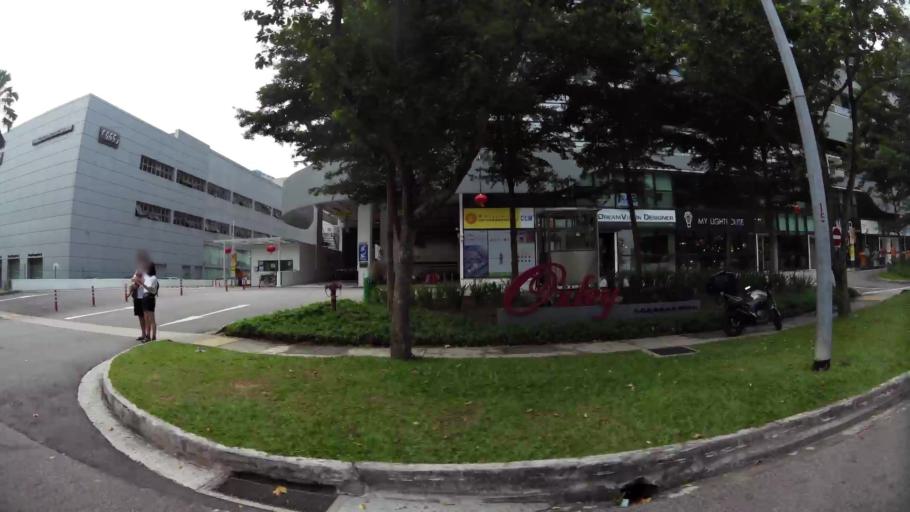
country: SG
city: Singapore
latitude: 1.3321
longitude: 103.8912
